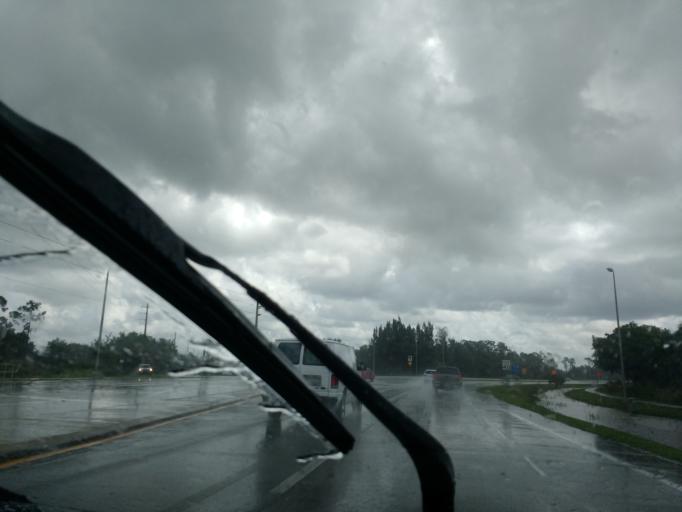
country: US
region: Florida
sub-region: Charlotte County
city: Charlotte Park
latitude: 26.8920
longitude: -82.0231
